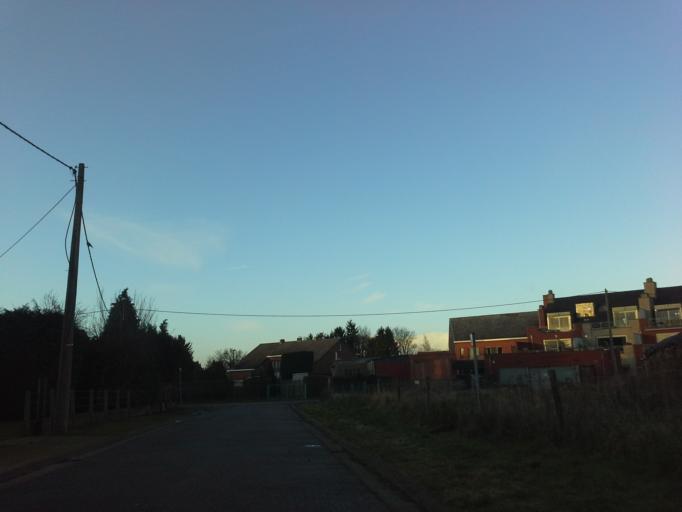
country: BE
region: Flanders
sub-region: Provincie Antwerpen
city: Meerhout
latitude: 51.1326
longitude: 5.0709
